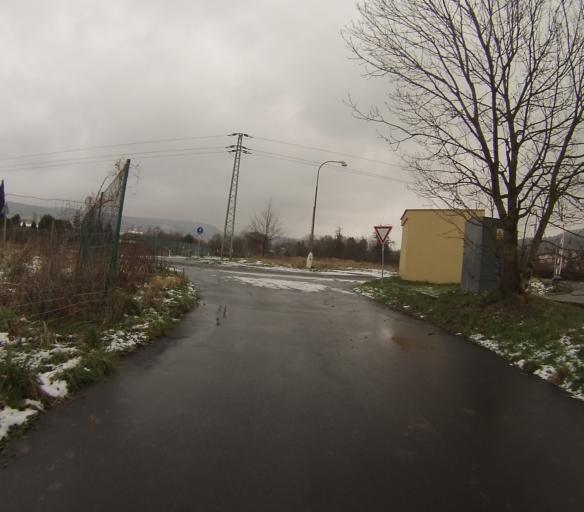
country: CZ
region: Ustecky
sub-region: Okres Decin
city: Decin
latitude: 50.7546
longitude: 14.2004
